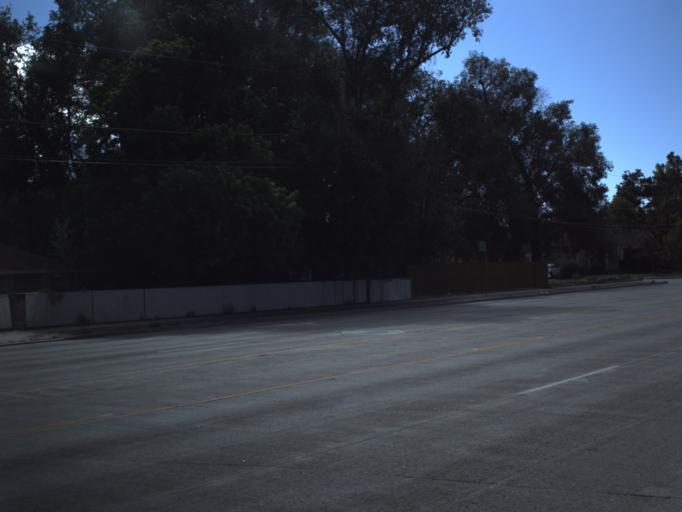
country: US
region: Utah
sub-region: Salt Lake County
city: West Jordan
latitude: 40.5931
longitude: -111.9389
